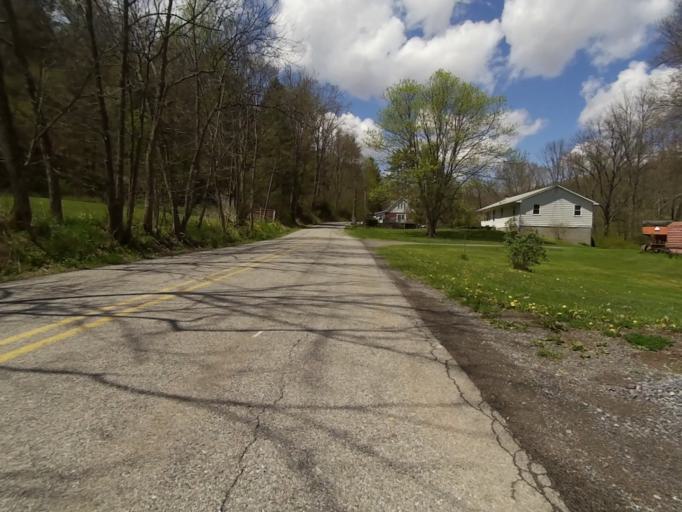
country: US
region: Pennsylvania
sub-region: Centre County
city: Milesburg
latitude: 40.9428
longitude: -77.8812
